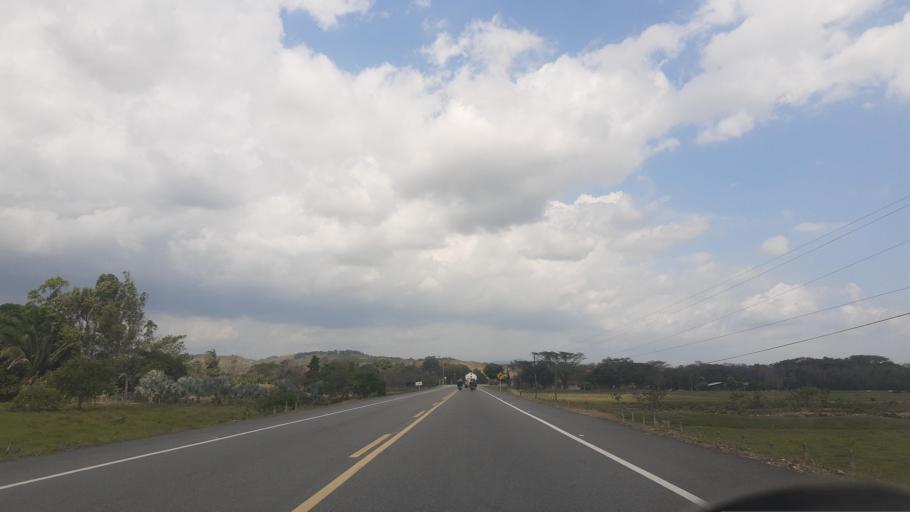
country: CO
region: Casanare
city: Tauramena
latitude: 4.9134
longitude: -72.6757
